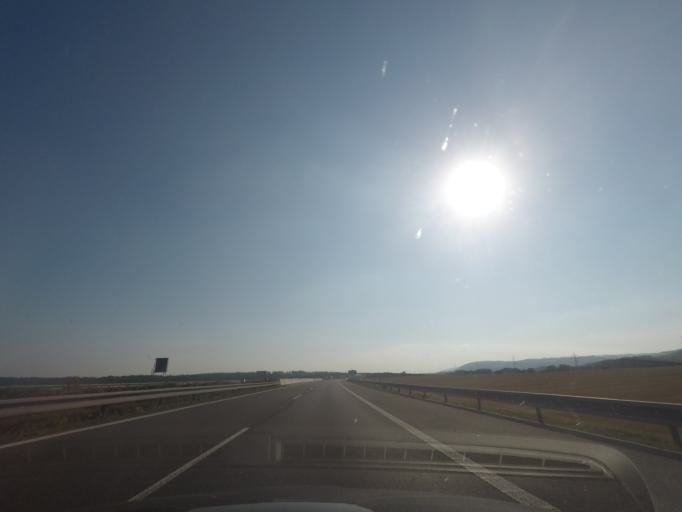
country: CZ
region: Olomoucky
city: Belotin
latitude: 49.5911
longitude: 17.7799
